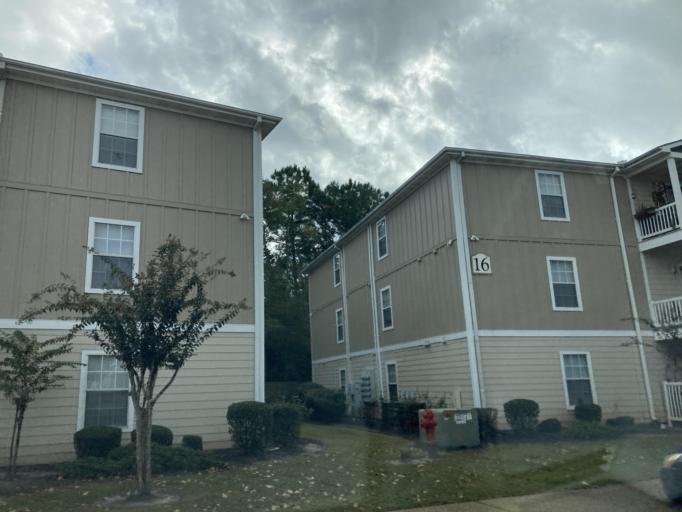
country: US
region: Mississippi
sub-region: Jackson County
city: Gulf Hills
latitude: 30.4363
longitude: -88.8365
